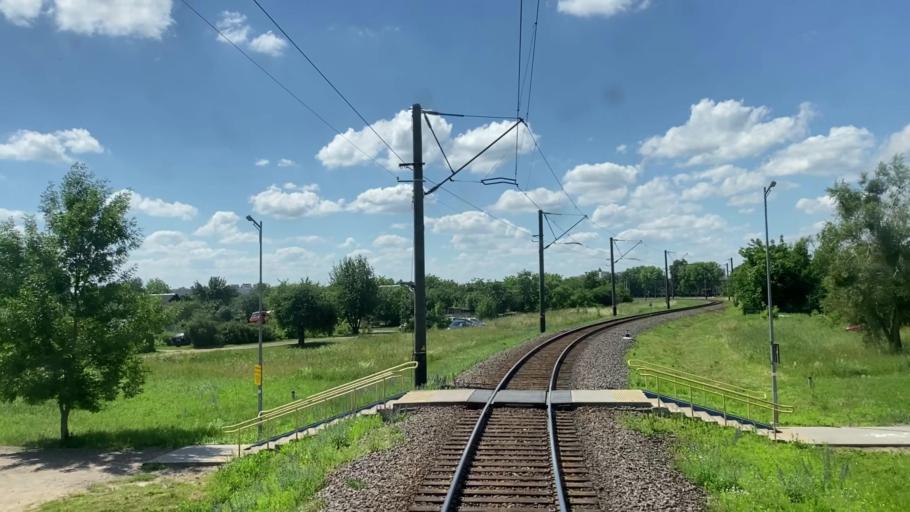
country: BY
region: Brest
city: Baranovichi
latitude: 53.1432
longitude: 26.0338
